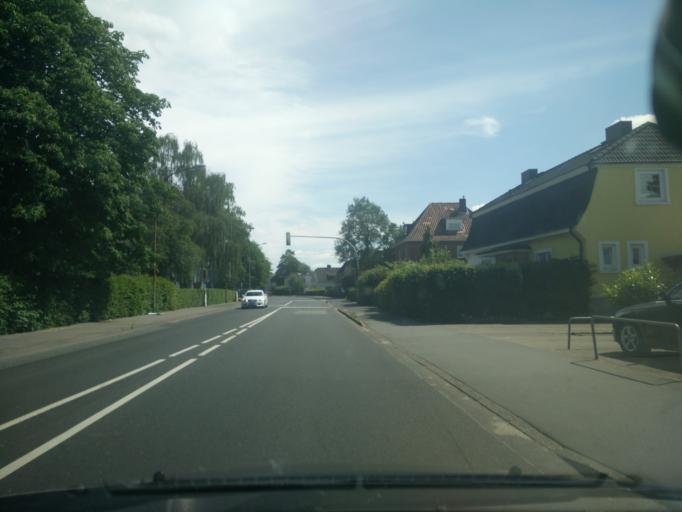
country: DE
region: Schleswig-Holstein
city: Tornesch
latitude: 53.6949
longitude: 9.7145
